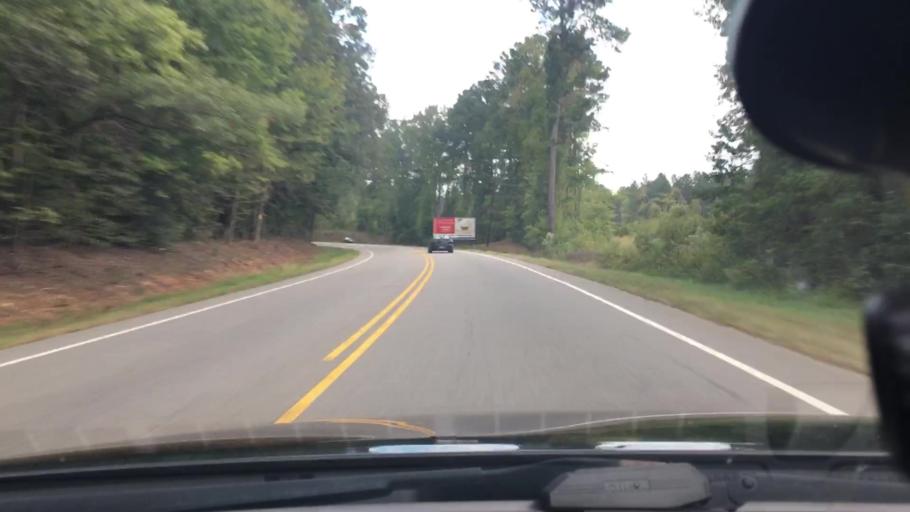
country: US
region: North Carolina
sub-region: Moore County
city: Carthage
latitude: 35.3626
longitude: -79.4418
